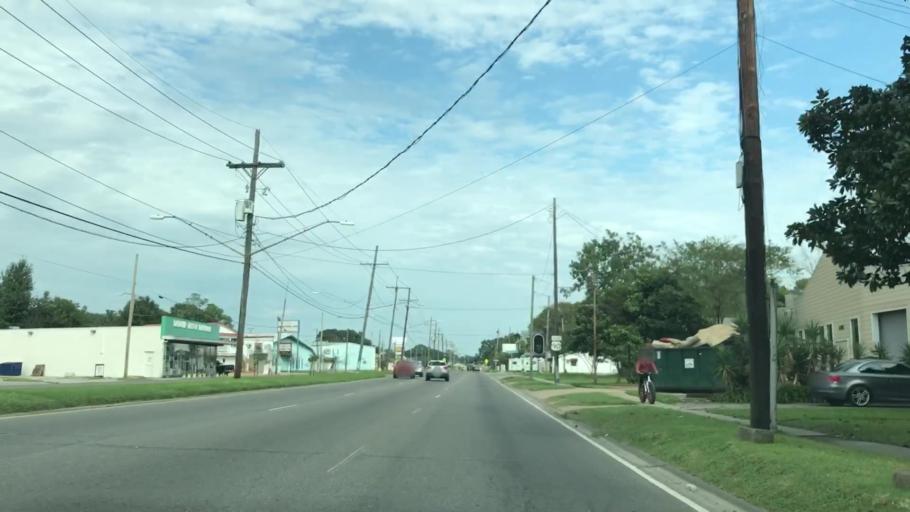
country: US
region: Louisiana
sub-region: Jefferson Parish
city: Elmwood
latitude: 29.9598
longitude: -90.1715
